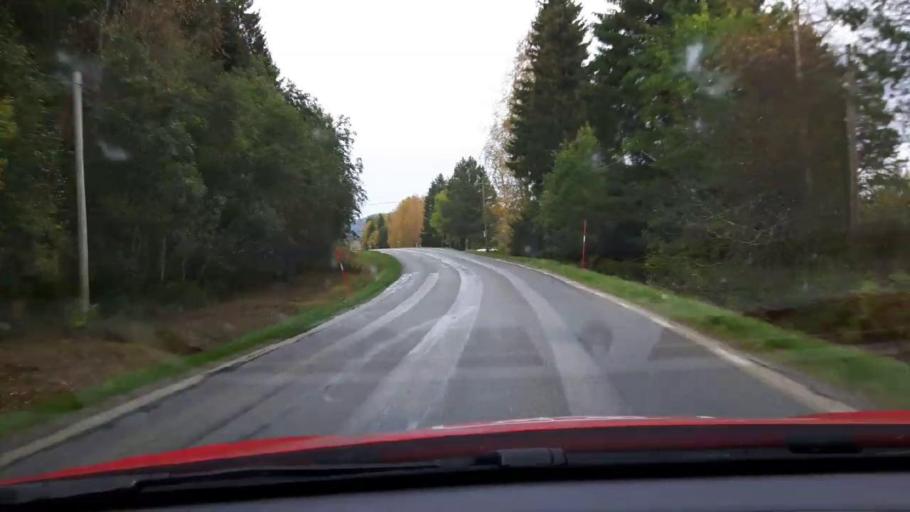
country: SE
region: Jaemtland
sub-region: Bergs Kommun
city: Hoverberg
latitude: 62.7875
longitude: 14.4371
